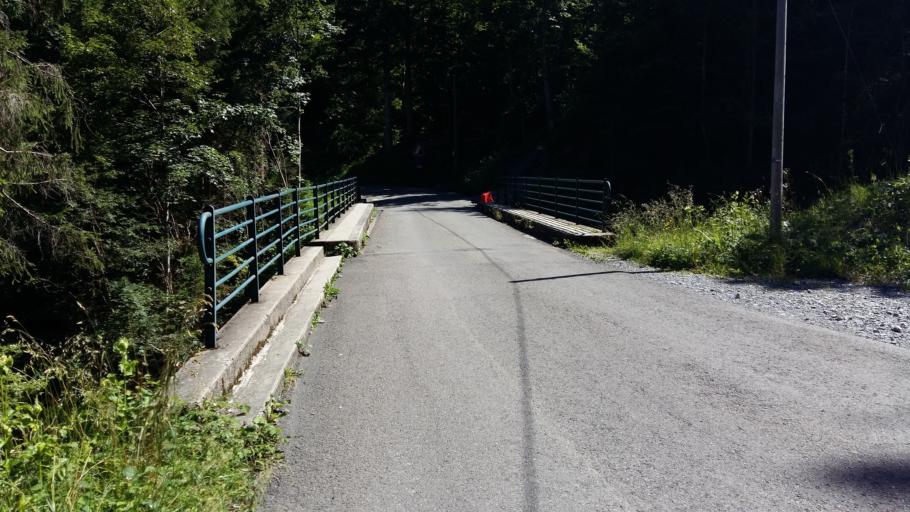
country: FR
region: Rhone-Alpes
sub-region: Departement de la Haute-Savoie
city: Samoens
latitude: 46.0291
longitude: 6.7710
